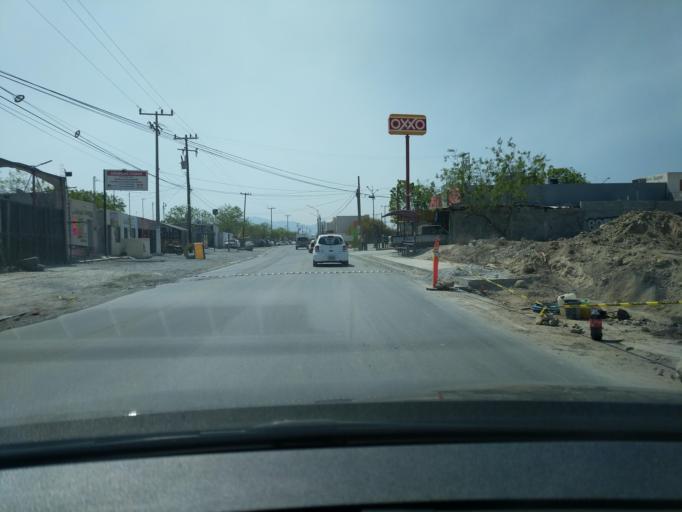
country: MX
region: Nuevo Leon
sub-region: Garcia
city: Valle de Lincoln
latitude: 25.7931
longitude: -100.4737
